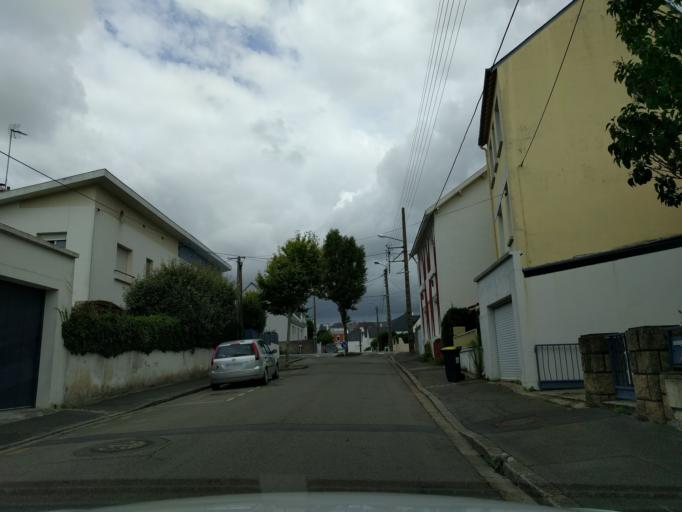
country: FR
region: Brittany
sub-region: Departement du Morbihan
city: Lorient
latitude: 47.7383
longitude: -3.3873
